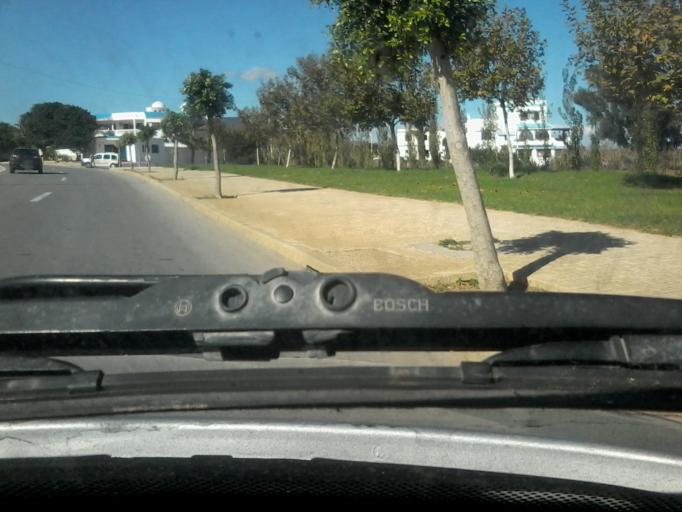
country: MA
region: Tanger-Tetouan
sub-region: Tetouan
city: Martil
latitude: 35.6948
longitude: -5.3335
